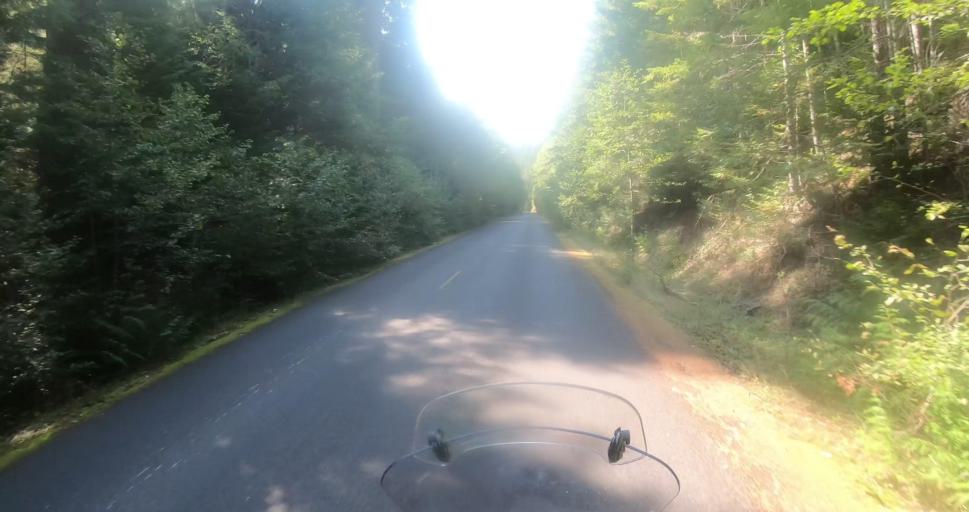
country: US
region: Washington
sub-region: Skamania County
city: Carson
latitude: 46.1724
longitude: -121.8607
